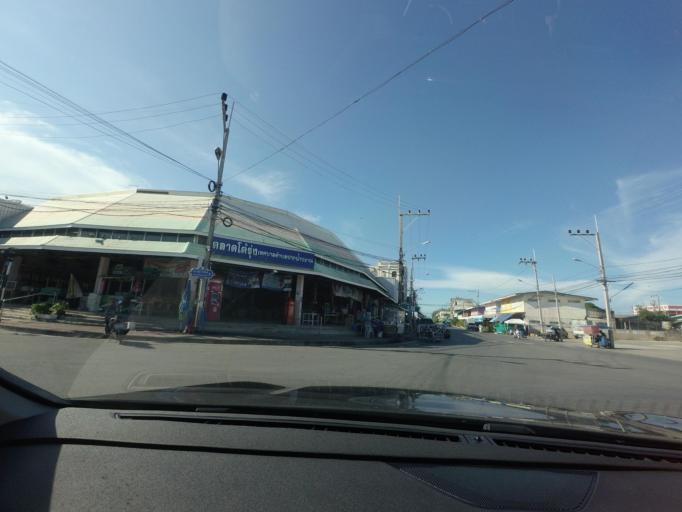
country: TH
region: Prachuap Khiri Khan
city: Pran Buri
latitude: 12.4025
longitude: 99.9917
